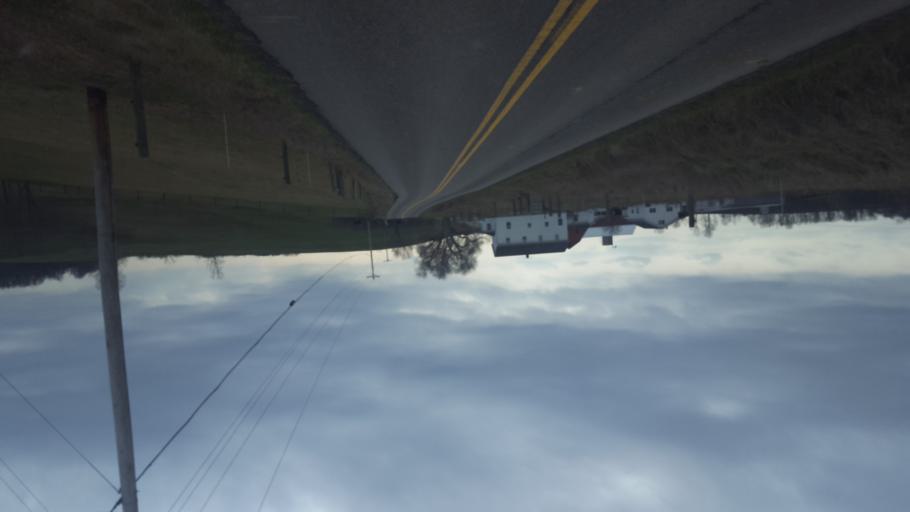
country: US
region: Ohio
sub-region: Gallia County
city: Gallipolis
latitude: 38.7572
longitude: -82.3711
